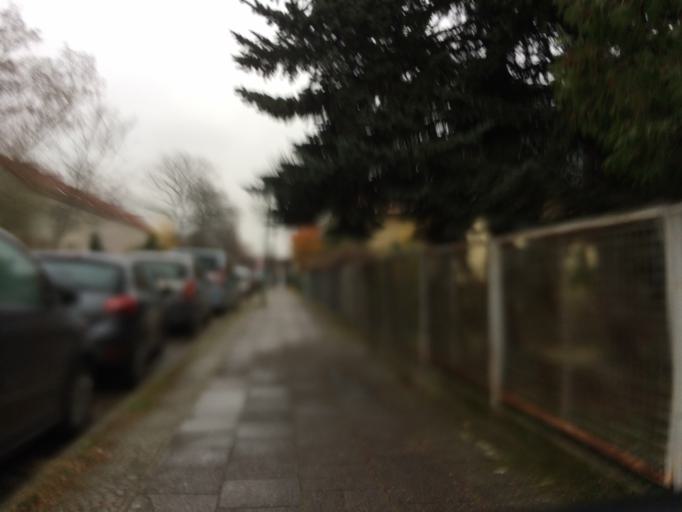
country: DE
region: Berlin
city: Niederschonhausen
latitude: 52.5791
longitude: 13.4013
